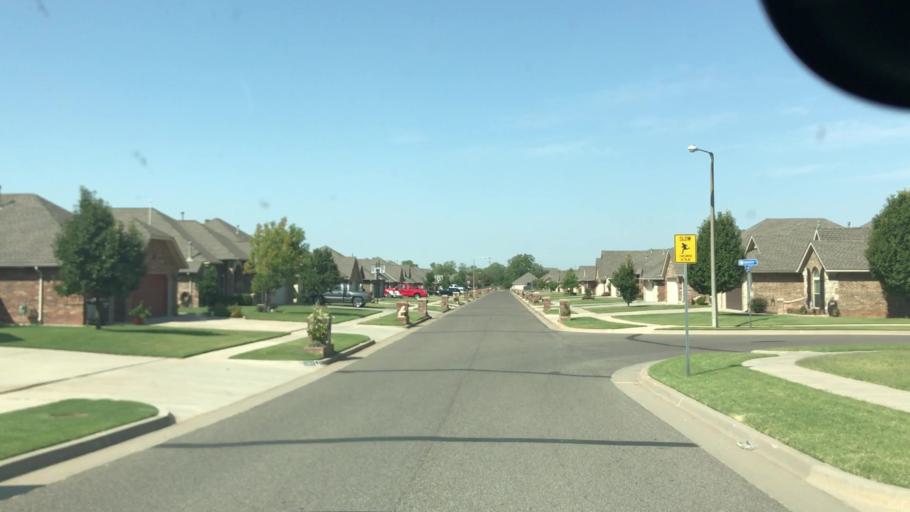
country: US
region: Oklahoma
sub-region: Cleveland County
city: Moore
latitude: 35.3513
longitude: -97.5124
